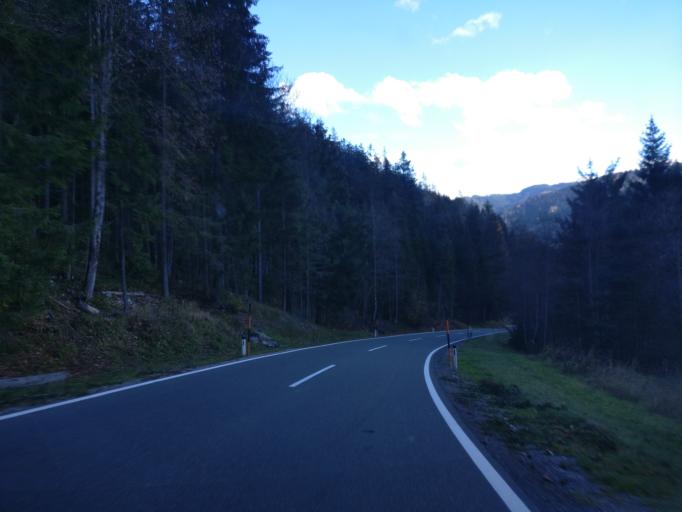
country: AT
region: Salzburg
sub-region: Politischer Bezirk Sankt Johann im Pongau
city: Muhlbach am Hochkonig
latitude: 47.3877
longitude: 13.1020
